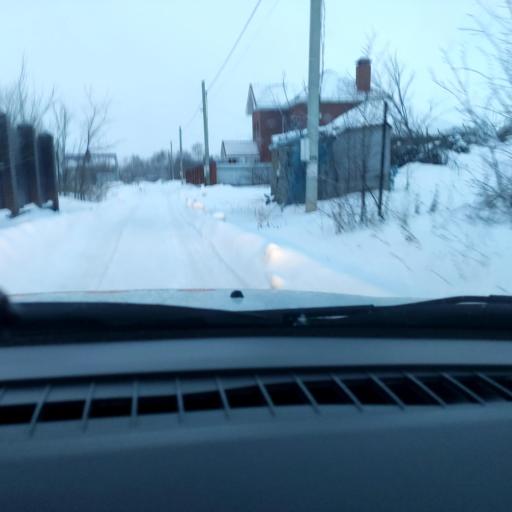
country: RU
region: Samara
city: Dubovyy Umet
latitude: 53.0286
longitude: 50.2302
